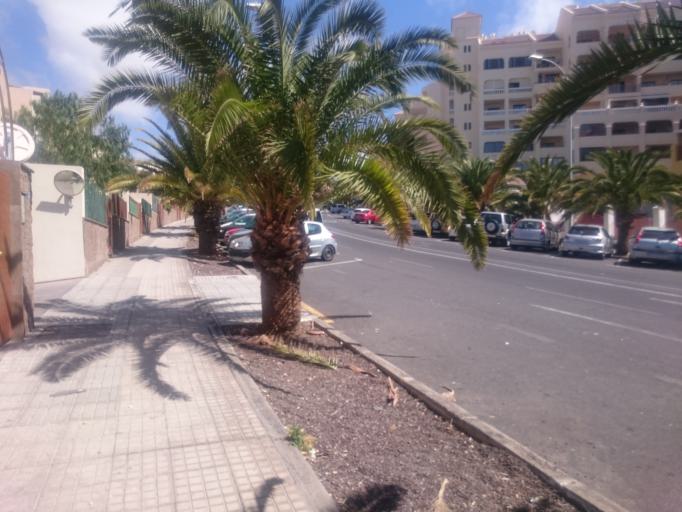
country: ES
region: Canary Islands
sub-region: Provincia de Santa Cruz de Tenerife
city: Playa de las Americas
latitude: 28.0553
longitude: -16.7056
